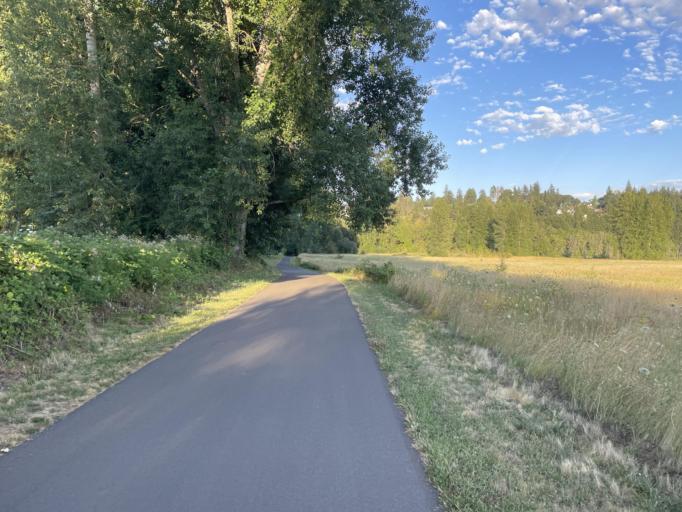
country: US
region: Oregon
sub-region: Marion County
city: Salem
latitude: 44.9265
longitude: -123.0617
